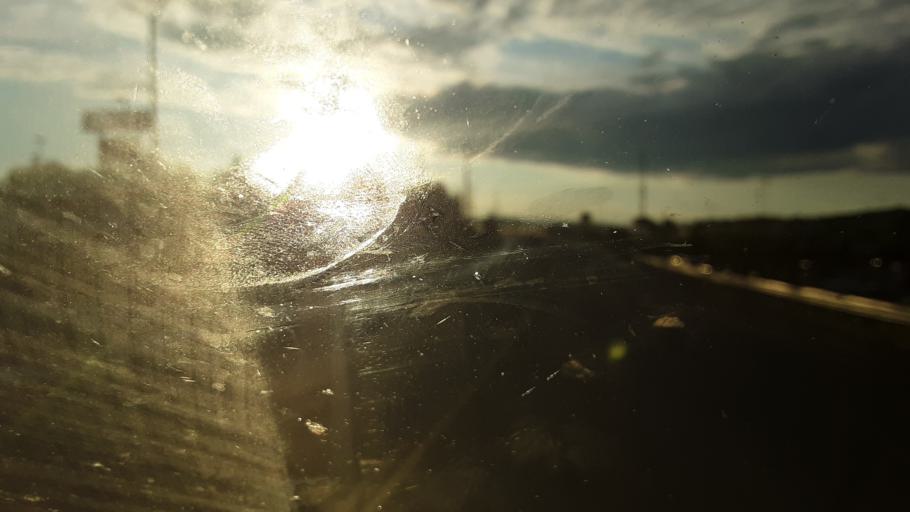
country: US
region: Maine
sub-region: Aroostook County
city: Presque Isle
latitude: 46.6950
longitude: -67.9998
